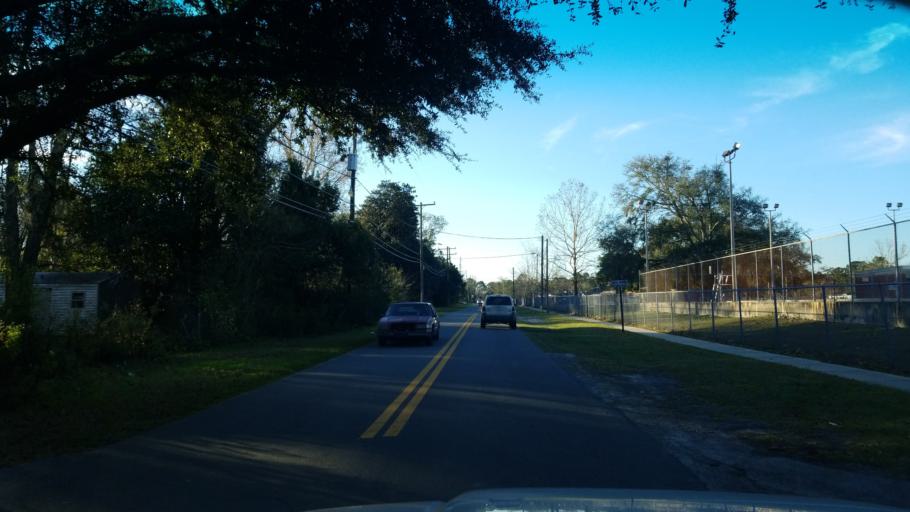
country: US
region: Florida
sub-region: Duval County
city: Jacksonville
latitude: 30.3283
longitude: -81.7860
